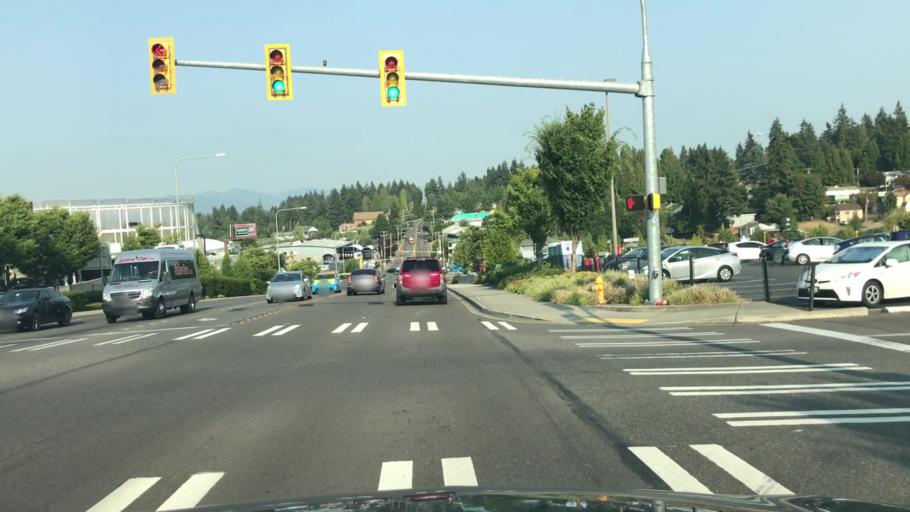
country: US
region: Washington
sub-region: King County
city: SeaTac
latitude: 47.4596
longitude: -122.2955
